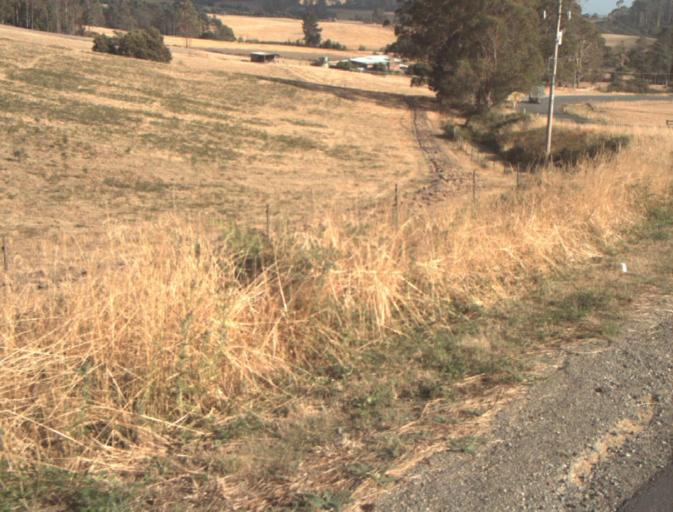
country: AU
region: Tasmania
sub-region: Launceston
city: Mayfield
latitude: -41.2021
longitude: 147.2181
